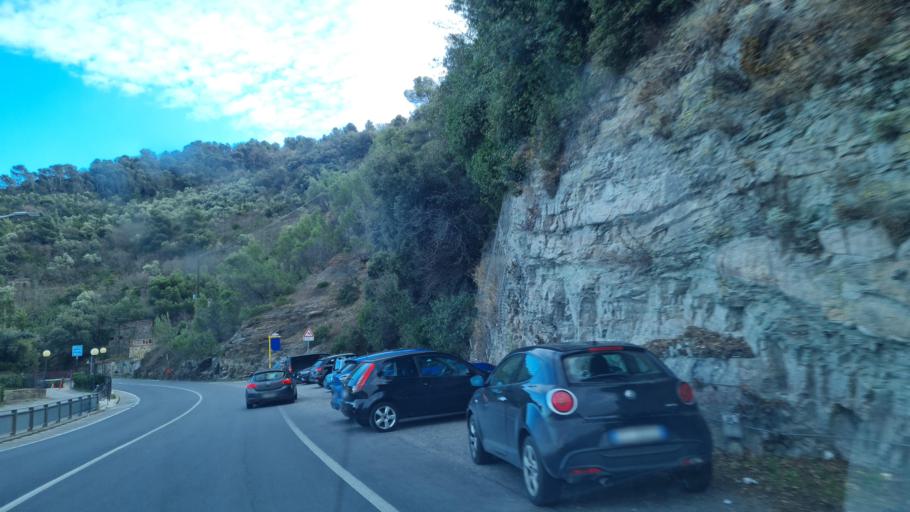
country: IT
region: Liguria
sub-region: Provincia di Savona
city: Noli
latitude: 44.1990
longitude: 8.4190
